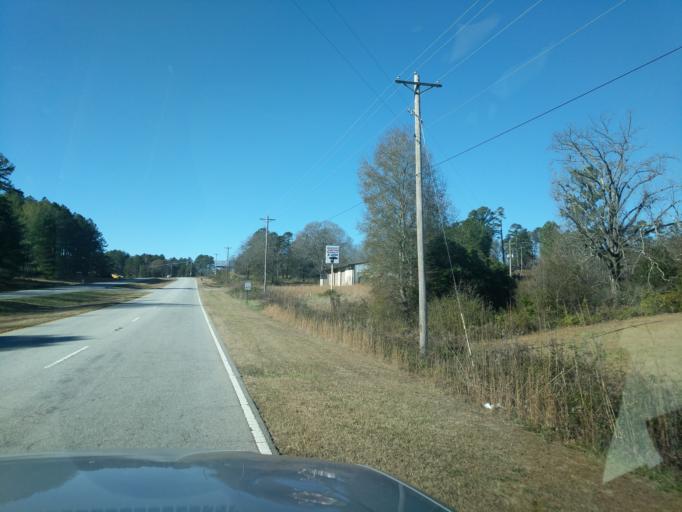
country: US
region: South Carolina
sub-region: Oconee County
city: Westminster
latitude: 34.6662
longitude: -83.0615
